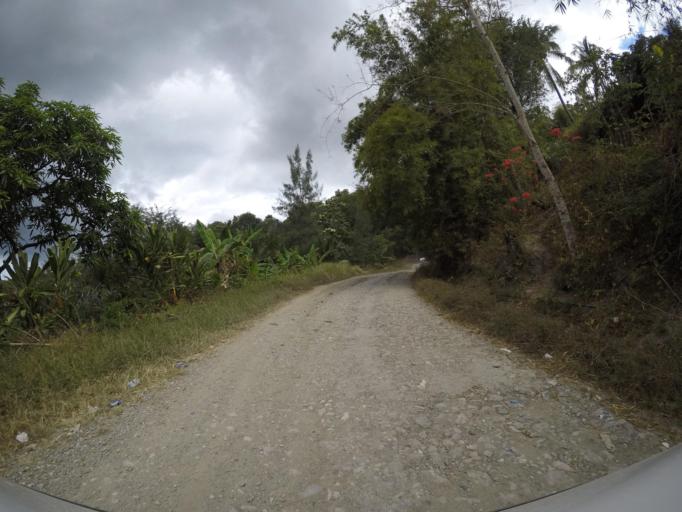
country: TL
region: Baucau
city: Baucau
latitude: -8.6266
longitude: 126.6562
